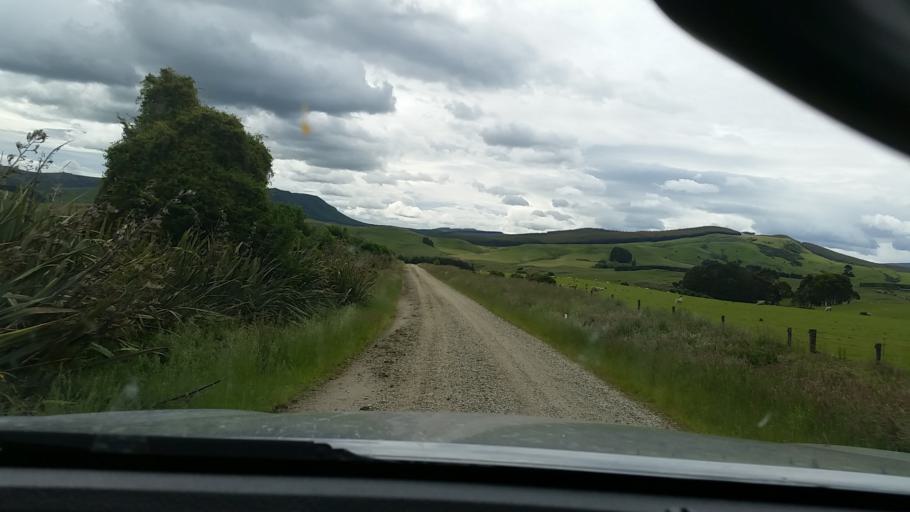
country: NZ
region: Southland
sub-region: Gore District
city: Gore
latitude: -46.2612
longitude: 168.9875
